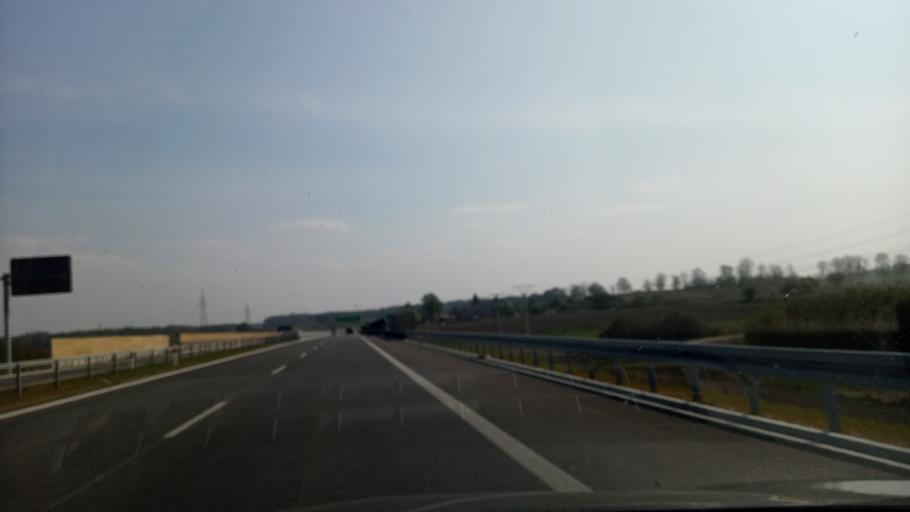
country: PL
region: West Pomeranian Voivodeship
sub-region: Powiat szczecinecki
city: Szczecinek
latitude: 53.6977
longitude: 16.7299
